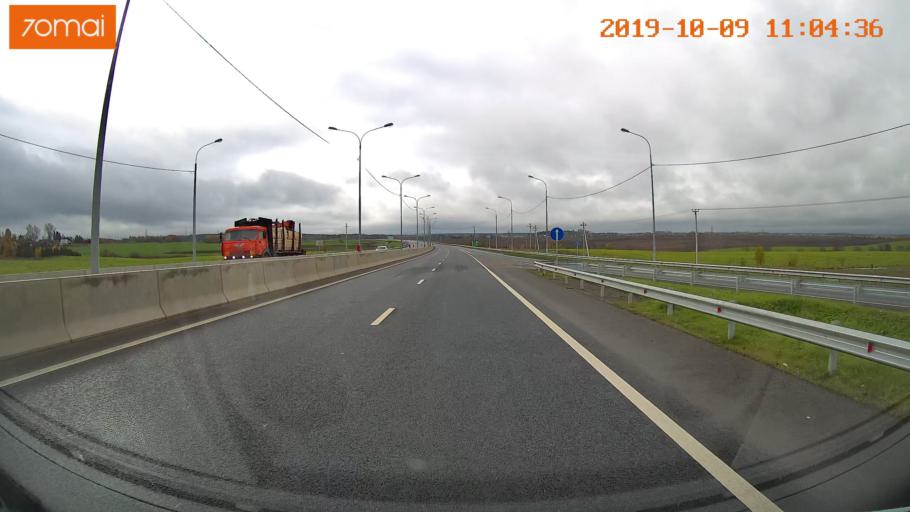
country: RU
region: Vologda
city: Vologda
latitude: 59.2106
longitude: 39.7660
